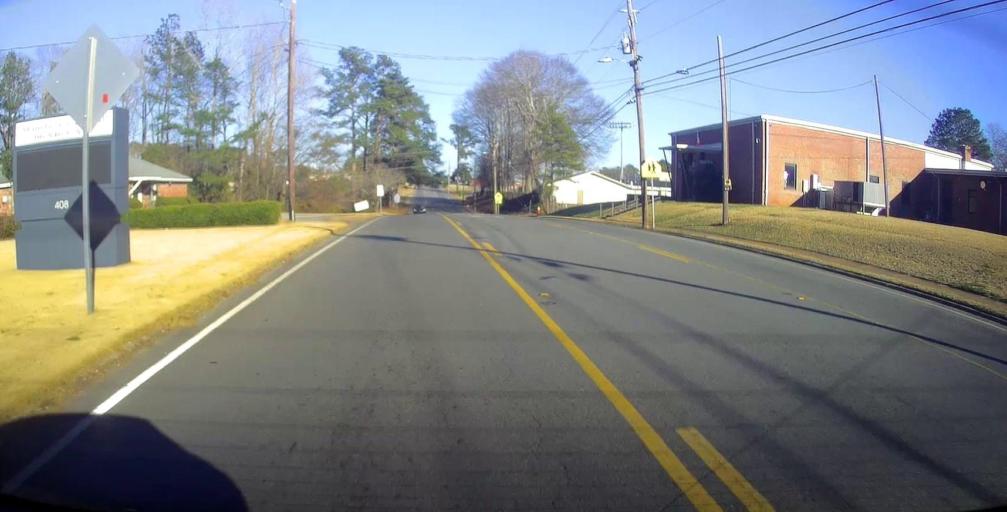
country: US
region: Georgia
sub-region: Meriwether County
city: Manchester
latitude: 32.8601
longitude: -84.6192
